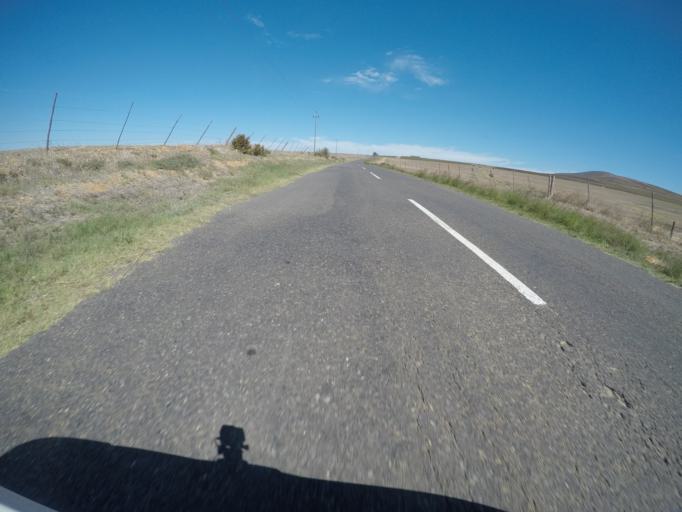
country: ZA
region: Western Cape
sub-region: City of Cape Town
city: Atlantis
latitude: -33.7046
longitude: 18.5863
